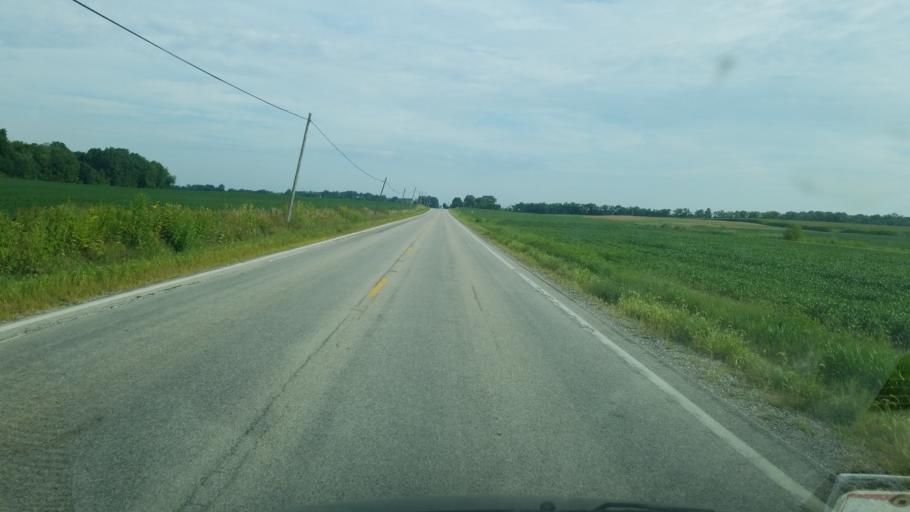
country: US
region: Ohio
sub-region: Crawford County
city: Bucyrus
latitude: 40.9146
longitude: -83.0167
